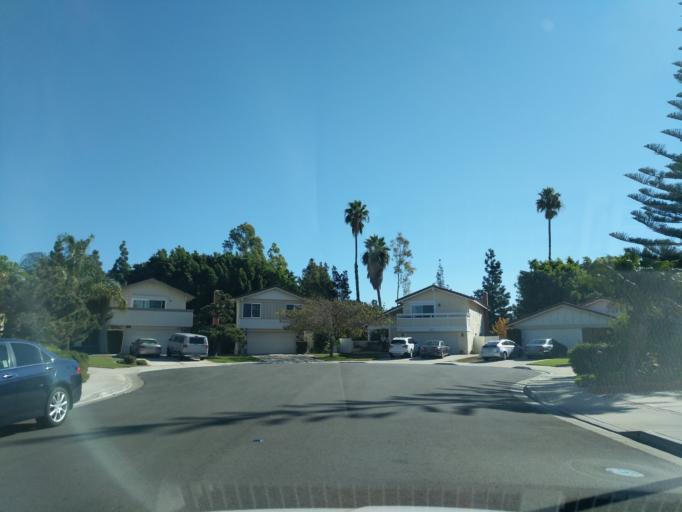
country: US
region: California
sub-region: Orange County
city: Irvine
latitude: 33.7009
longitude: -117.7931
